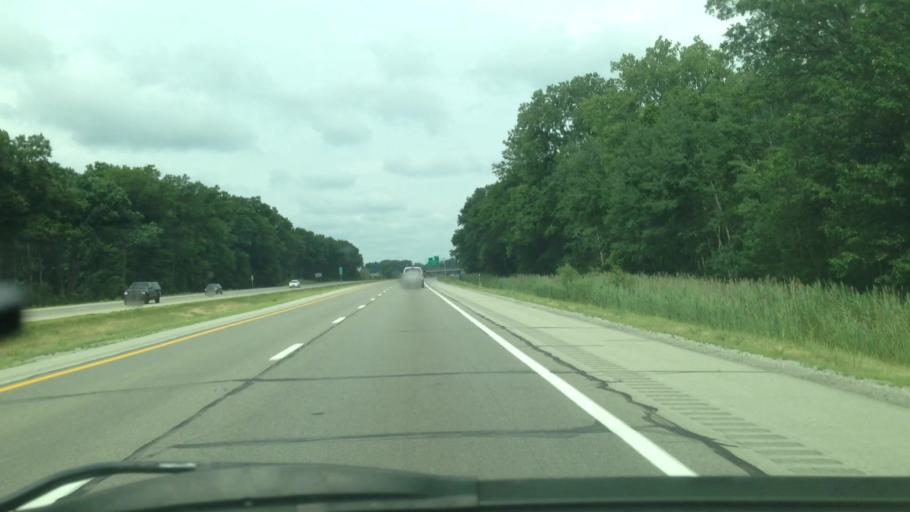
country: US
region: Ohio
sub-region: Lucas County
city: Holland
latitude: 41.5944
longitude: -83.7749
